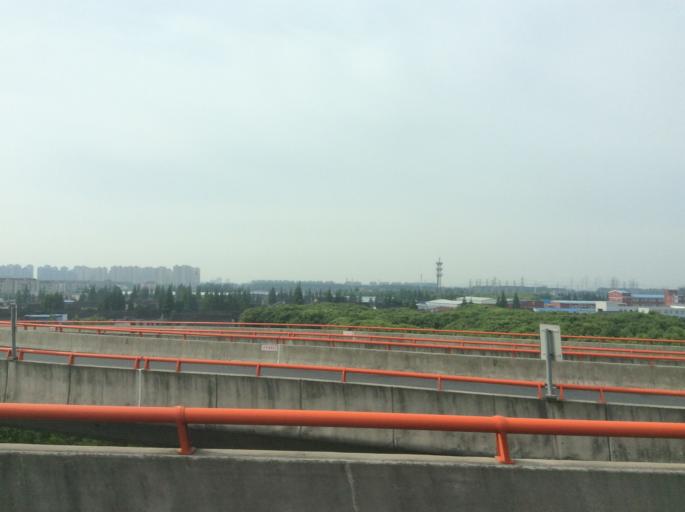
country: CN
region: Shanghai Shi
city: Changqiao
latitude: 31.1494
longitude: 121.4807
